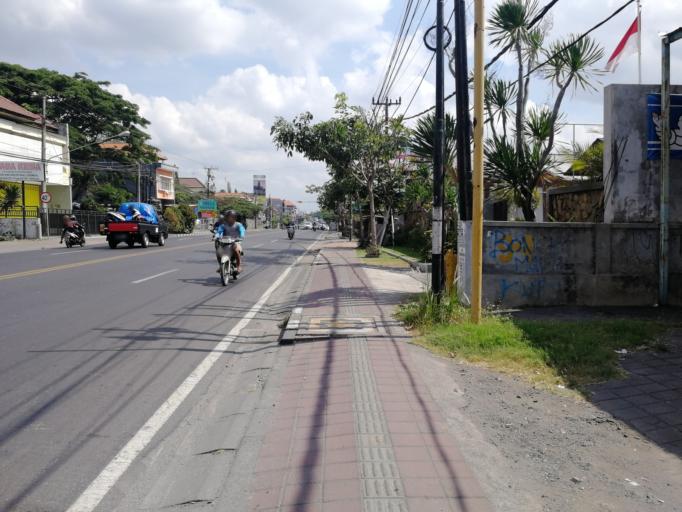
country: ID
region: Bali
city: Denpasar
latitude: -8.6425
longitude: 115.1963
